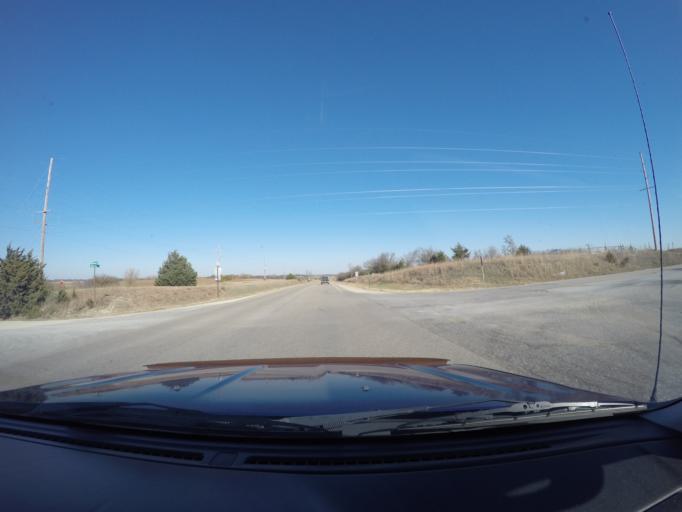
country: US
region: Kansas
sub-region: Riley County
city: Ogden
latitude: 39.3492
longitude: -96.7564
